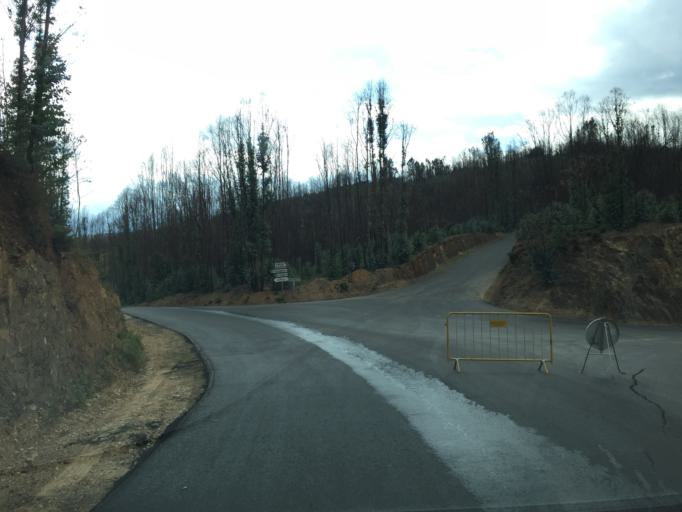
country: PT
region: Coimbra
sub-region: Pampilhosa da Serra
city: Pampilhosa da Serra
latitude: 40.0591
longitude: -8.0087
